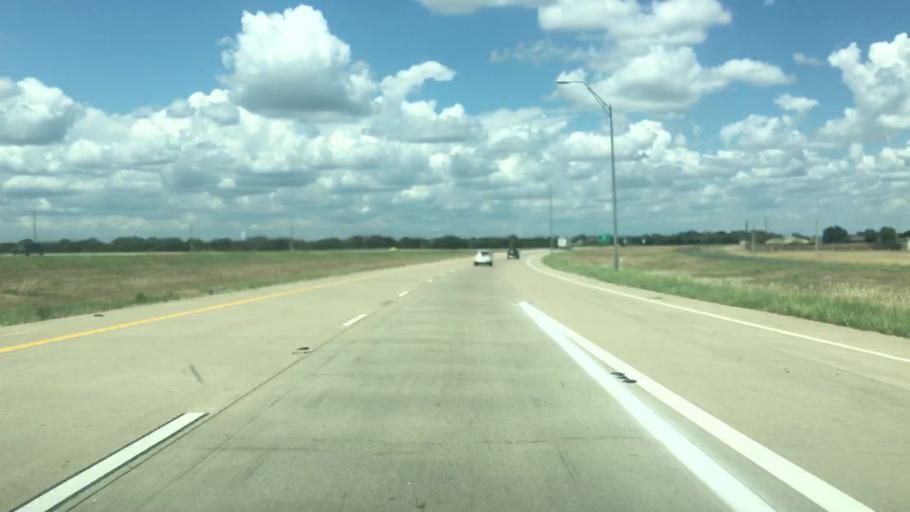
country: US
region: Texas
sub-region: Williamson County
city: Georgetown
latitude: 30.6267
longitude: -97.6247
